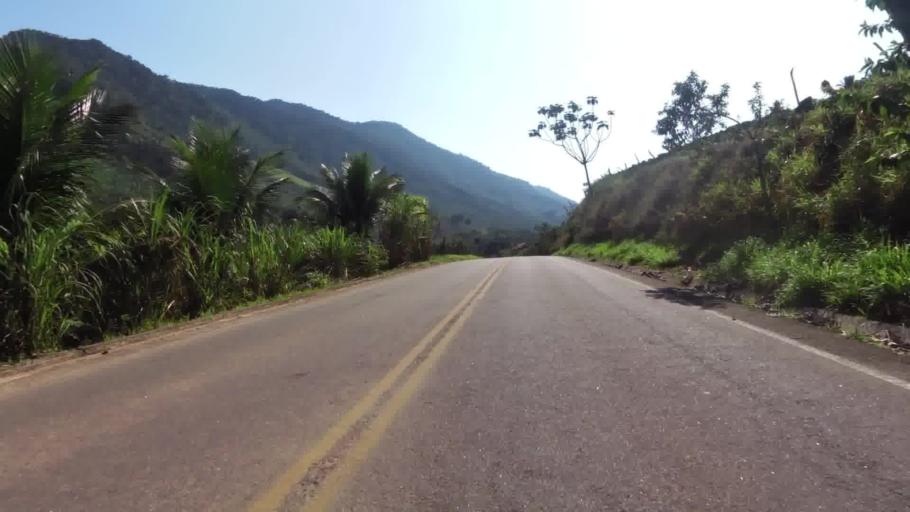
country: BR
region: Espirito Santo
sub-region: Alfredo Chaves
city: Alfredo Chaves
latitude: -20.6173
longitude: -40.7788
